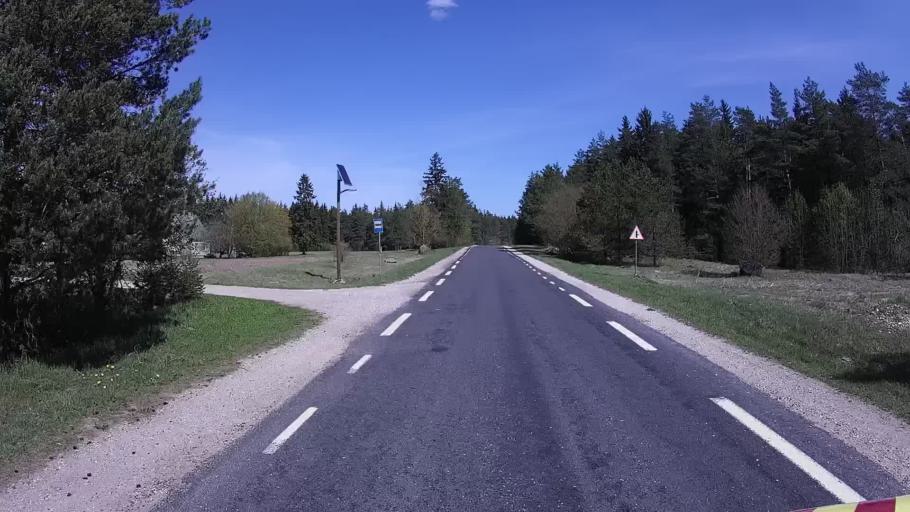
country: EE
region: Laeaene
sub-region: Ridala Parish
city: Uuemoisa
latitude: 59.0321
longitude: 23.8203
